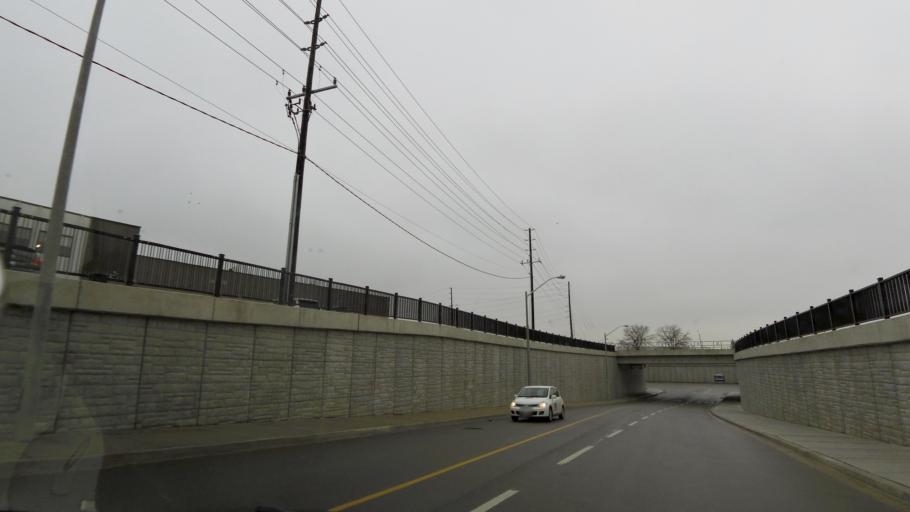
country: CA
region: Ontario
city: Etobicoke
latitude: 43.7048
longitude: -79.6035
